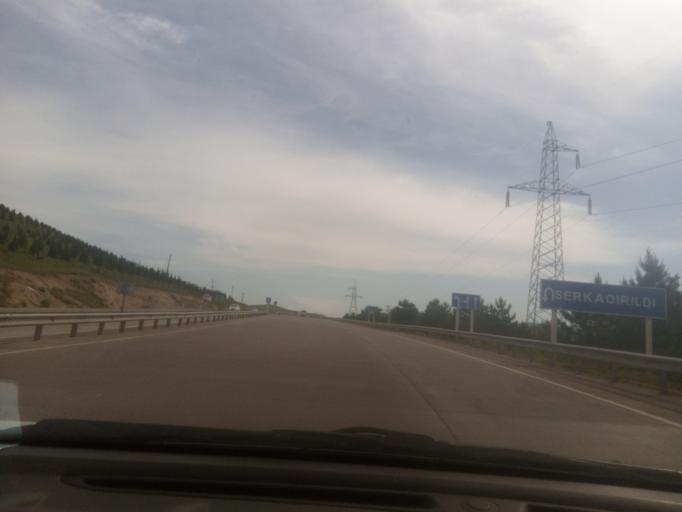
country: UZ
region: Toshkent
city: Angren
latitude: 41.0666
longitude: 70.2272
